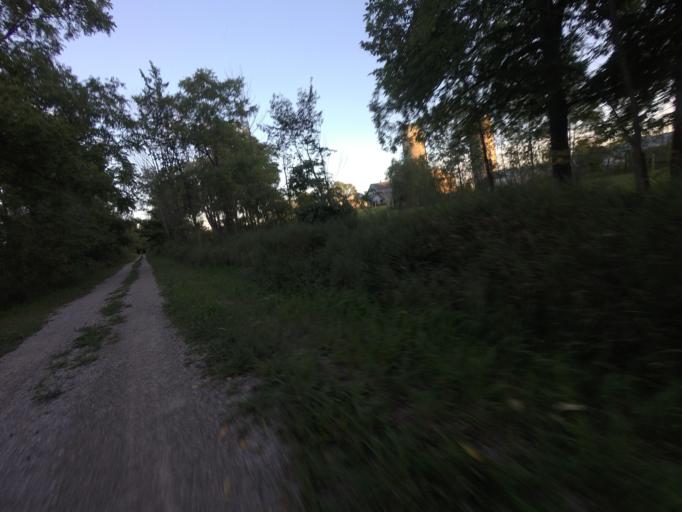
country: CA
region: Ontario
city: Goderich
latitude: 43.7511
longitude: -81.6607
